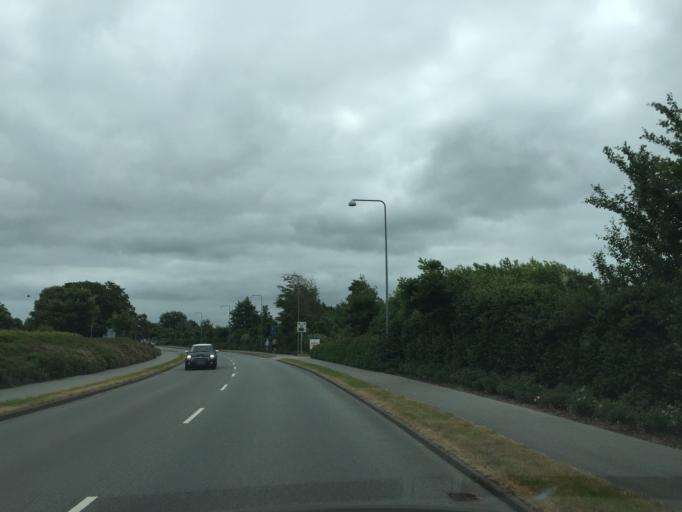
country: DK
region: South Denmark
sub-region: Tonder Kommune
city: Sherrebek
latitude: 55.1622
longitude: 8.7578
